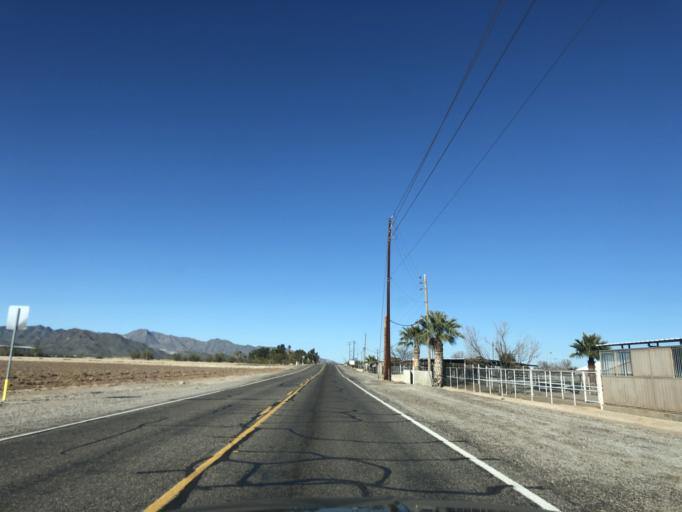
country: US
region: Arizona
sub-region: Maricopa County
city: Buckeye
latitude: 33.4267
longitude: -112.5042
